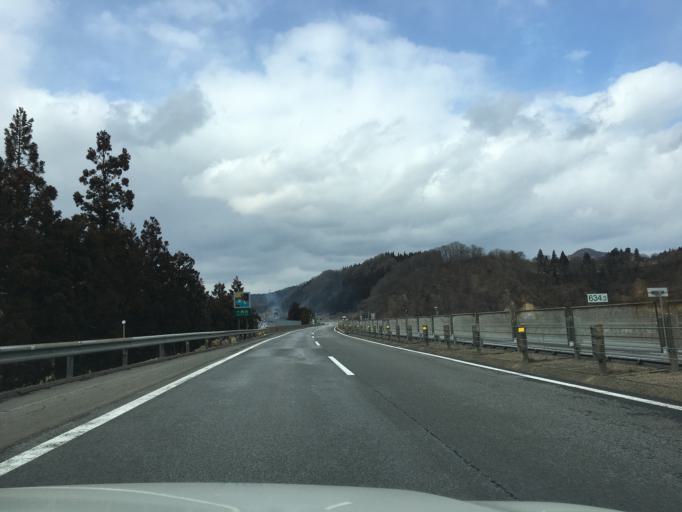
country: JP
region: Aomori
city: Kuroishi
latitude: 40.4970
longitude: 140.6238
